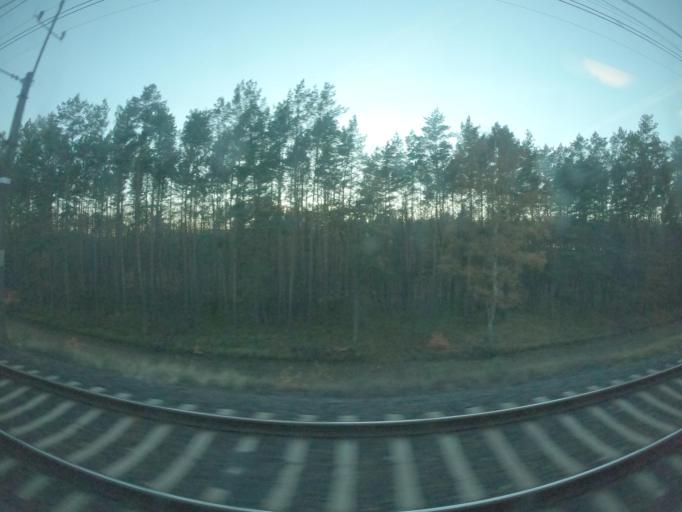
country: PL
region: West Pomeranian Voivodeship
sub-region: Powiat mysliborski
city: Boleszkowice
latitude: 52.7086
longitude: 14.5406
